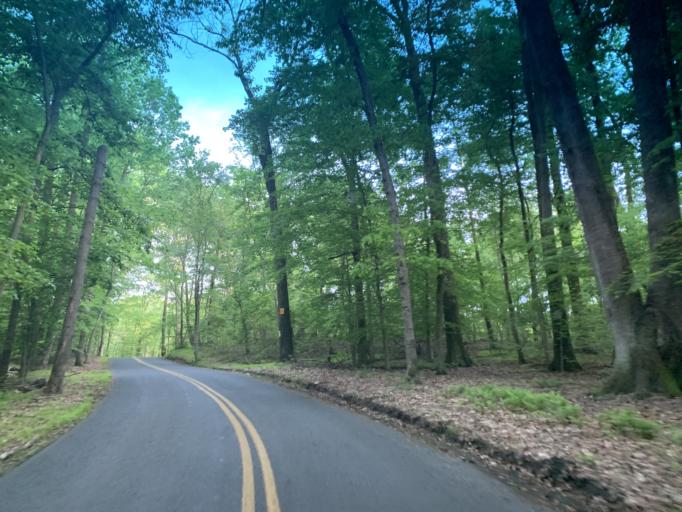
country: US
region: Pennsylvania
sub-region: York County
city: Susquehanna Trails
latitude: 39.6904
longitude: -76.2436
